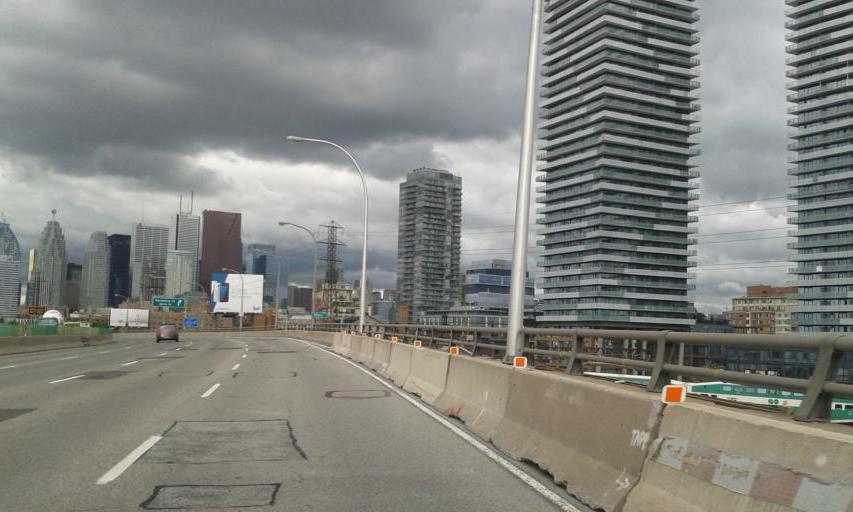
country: CA
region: Ontario
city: Toronto
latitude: 43.6492
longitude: -79.3556
